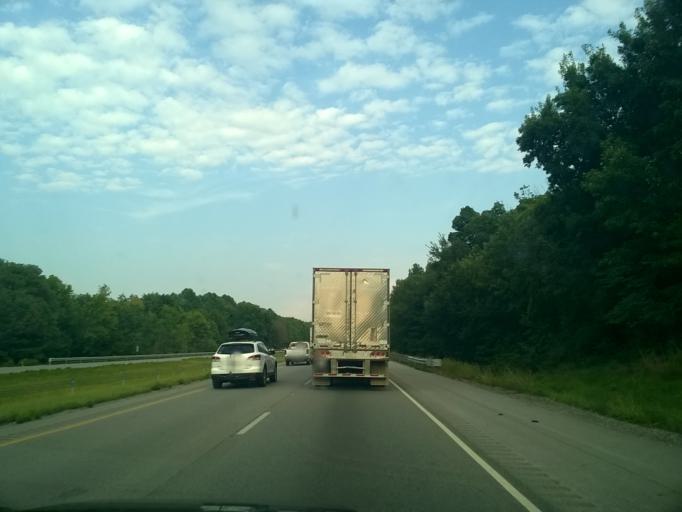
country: US
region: Indiana
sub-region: Putnam County
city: Cloverdale
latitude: 39.5329
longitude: -86.8439
